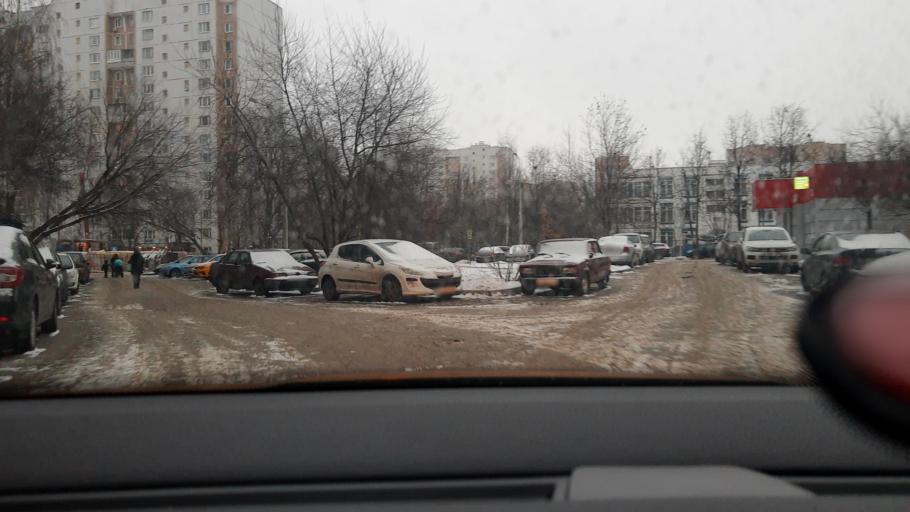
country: RU
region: Moscow
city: Solntsevo
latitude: 55.6392
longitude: 37.3582
